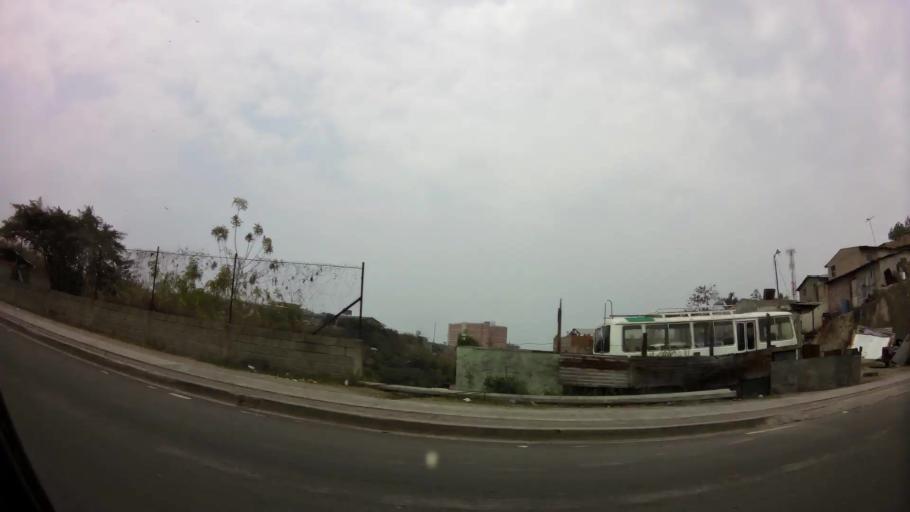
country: HN
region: Francisco Morazan
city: Yaguacire
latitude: 14.0553
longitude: -87.2537
